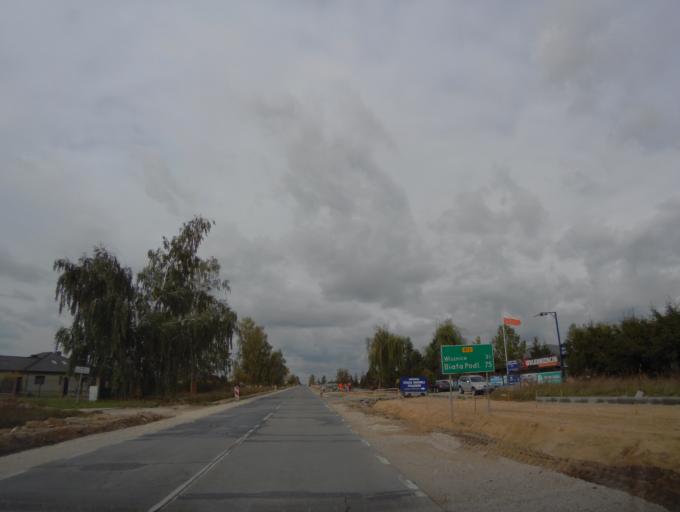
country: PL
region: Lublin Voivodeship
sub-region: Powiat wlodawski
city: Wlodawa
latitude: 51.5523
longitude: 23.5344
